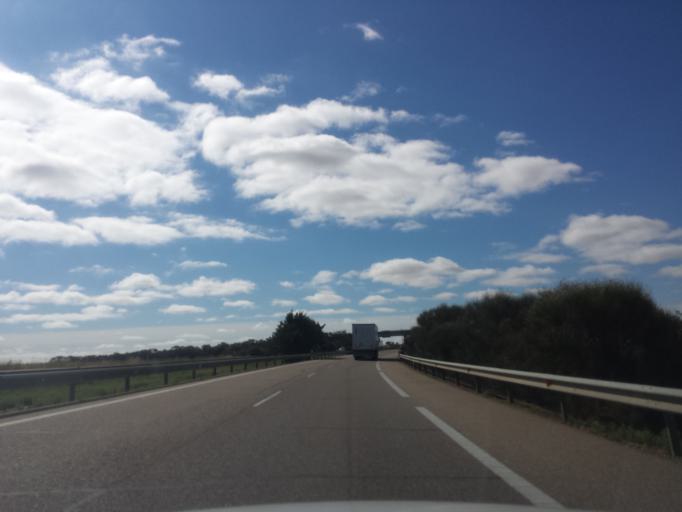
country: ES
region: Castille and Leon
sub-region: Provincia de Zamora
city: Cerecinos de Campos
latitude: 41.9004
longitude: -5.4760
